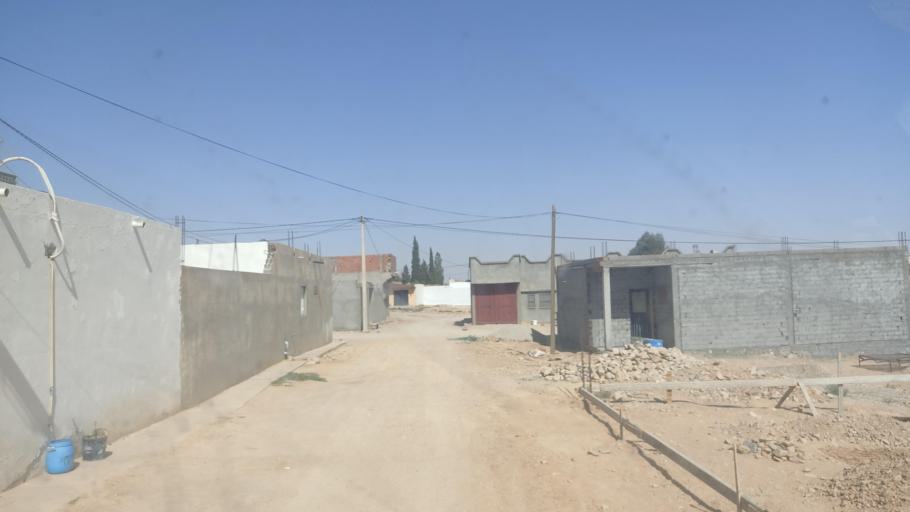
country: TN
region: Gafsa
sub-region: Gafsa Municipality
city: Gafsa
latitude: 34.3377
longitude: 8.9215
